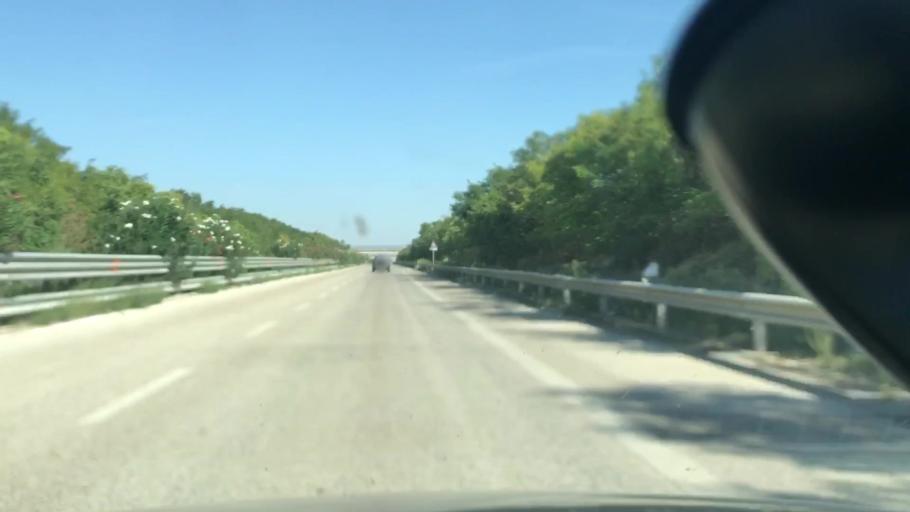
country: IT
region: Apulia
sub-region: Provincia di Foggia
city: Ordona
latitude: 41.2851
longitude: 15.5540
